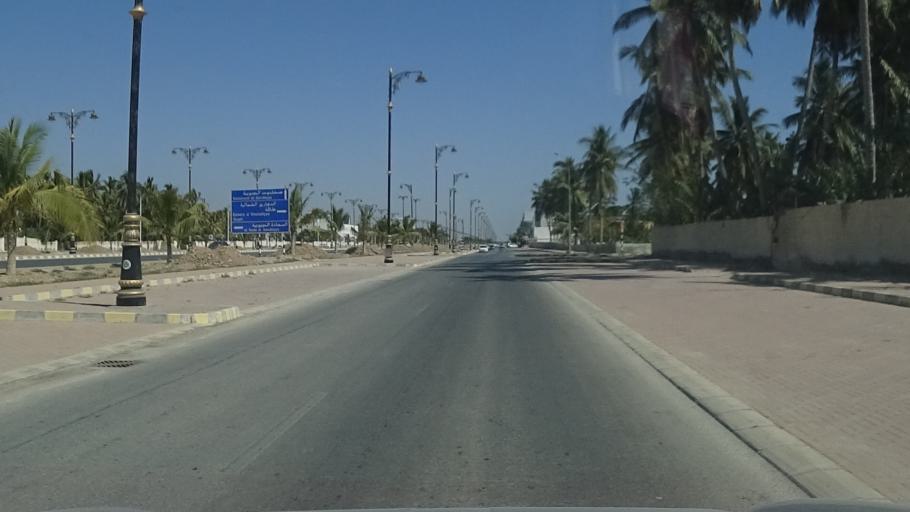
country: OM
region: Zufar
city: Salalah
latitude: 17.0360
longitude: 54.1570
